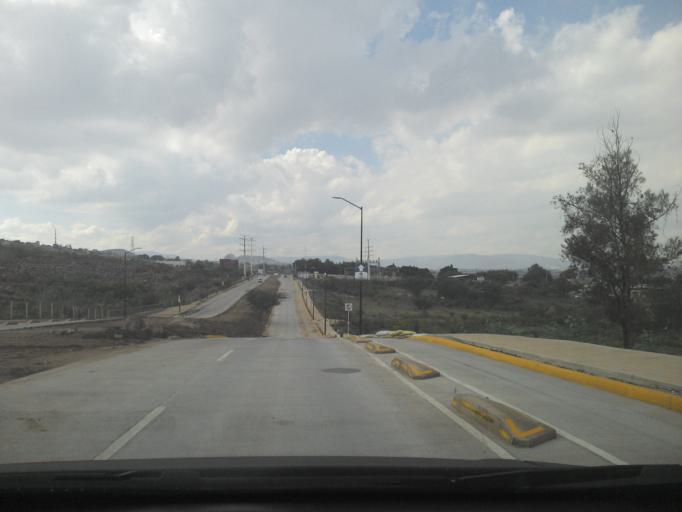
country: MX
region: Jalisco
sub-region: Tlajomulco de Zuniga
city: Altus Bosques
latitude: 20.6145
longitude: -103.3581
